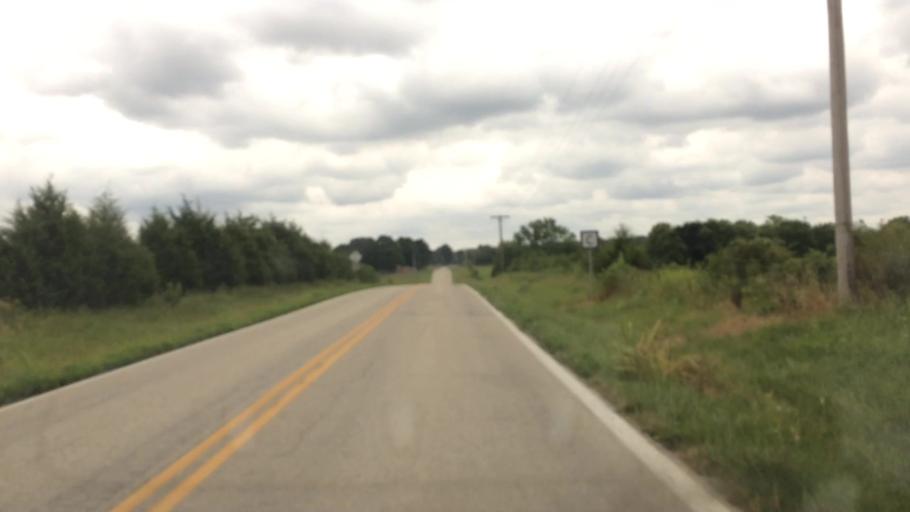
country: US
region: Missouri
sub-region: Greene County
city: Strafford
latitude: 37.2998
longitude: -93.1305
